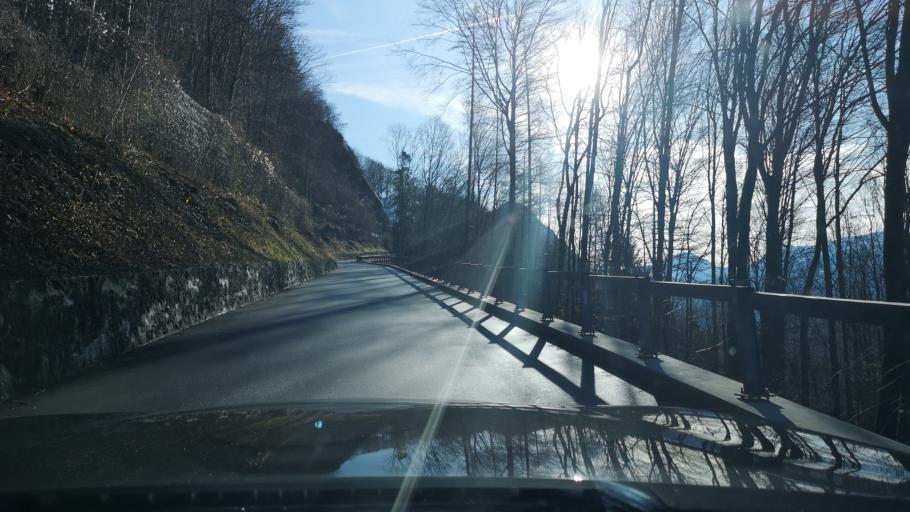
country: LI
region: Vaduz
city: Vaduz
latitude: 47.1329
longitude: 9.5296
